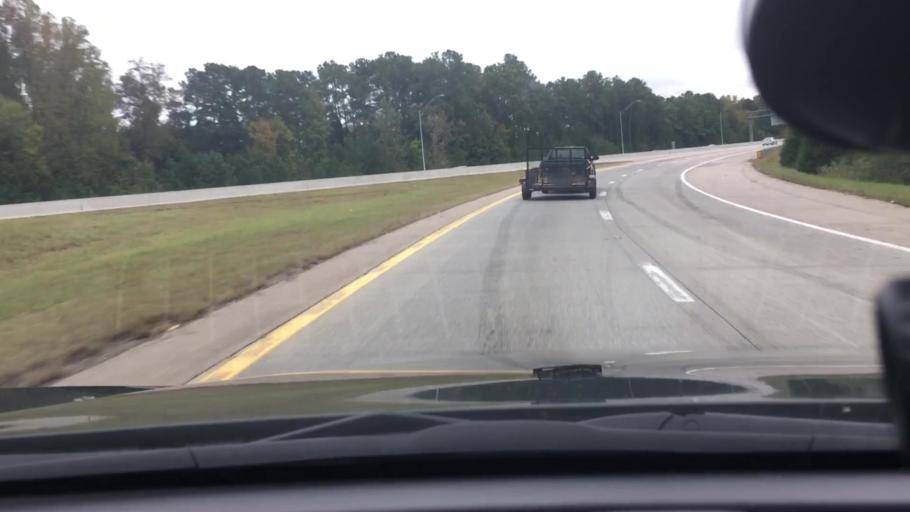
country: US
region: North Carolina
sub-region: Wake County
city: Raleigh
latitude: 35.7768
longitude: -78.5743
